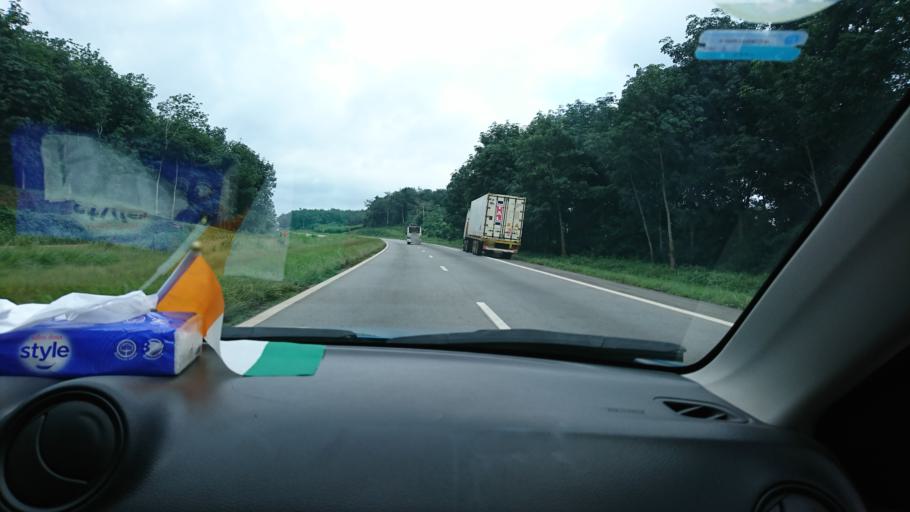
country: CI
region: Lagunes
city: Songon
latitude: 5.5361
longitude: -4.3008
